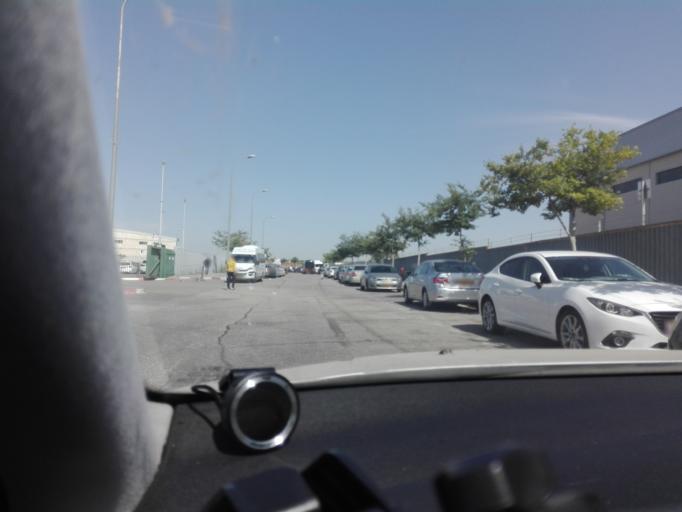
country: IL
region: Central District
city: Bene 'Ayish
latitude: 31.7209
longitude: 34.7603
